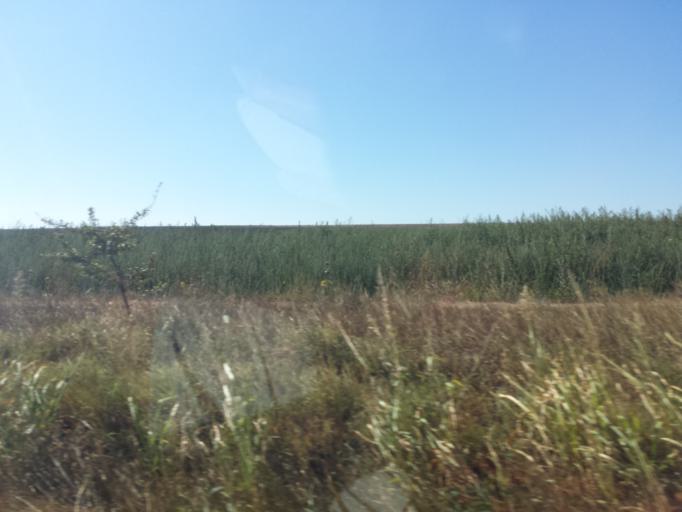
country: RO
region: Tulcea
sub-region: Comuna Frecatei
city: Cataloi
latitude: 45.1119
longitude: 28.7464
